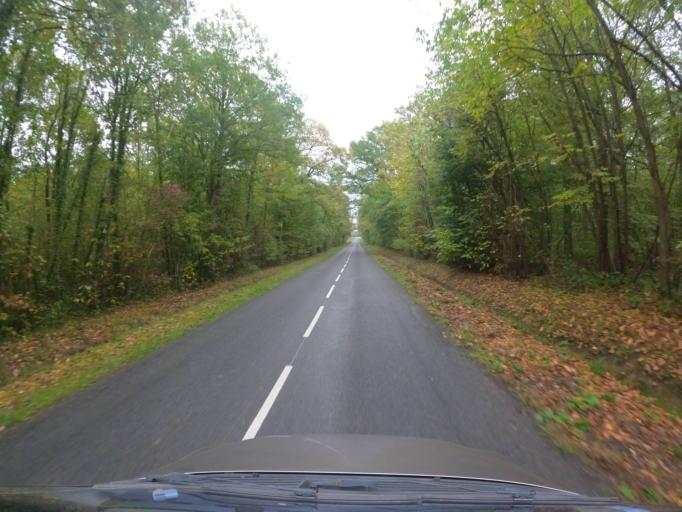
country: FR
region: Ile-de-France
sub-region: Departement de Seine-et-Marne
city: Serris
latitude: 48.8236
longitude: 2.7712
